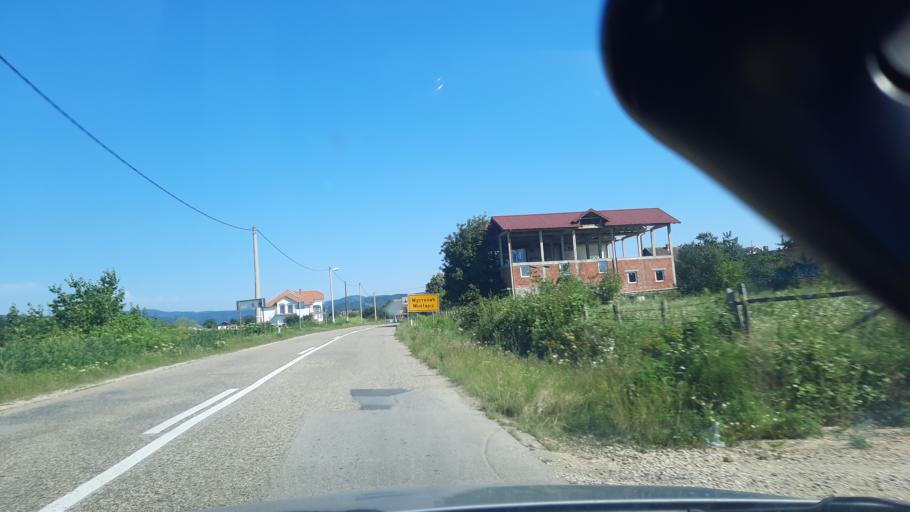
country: RS
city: Turija
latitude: 44.5550
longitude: 21.5442
